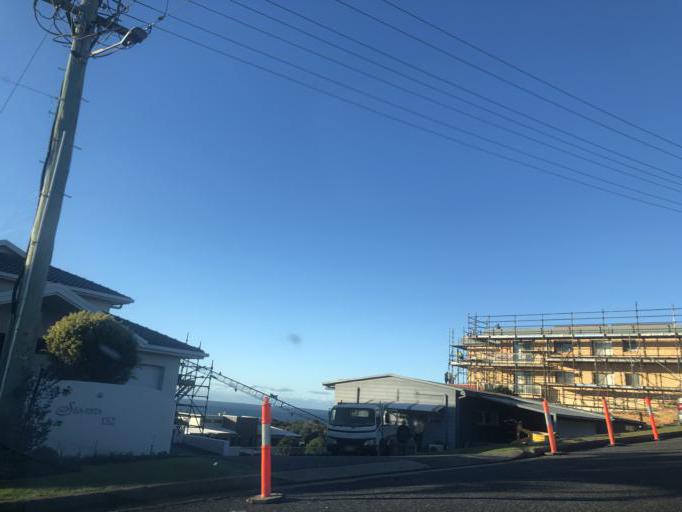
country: AU
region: New South Wales
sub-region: Coffs Harbour
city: Coffs Harbour
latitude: -30.3080
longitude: 153.1361
